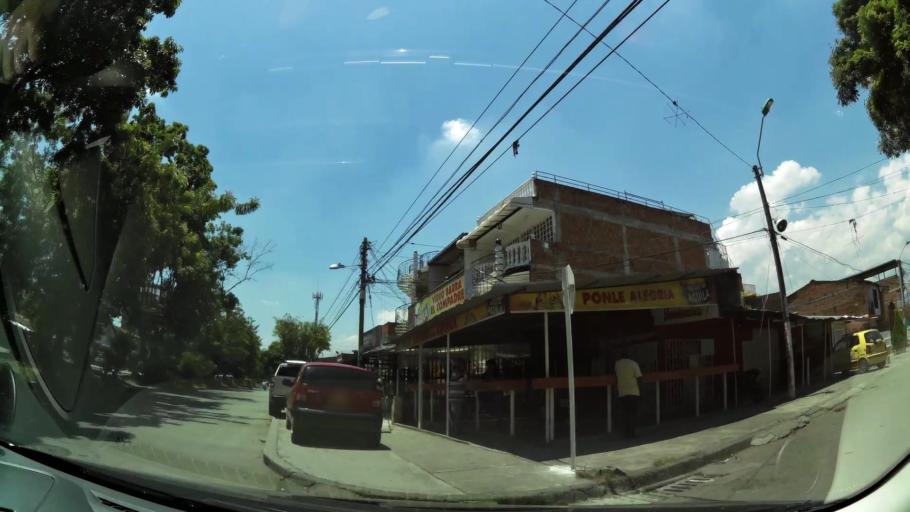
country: CO
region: Valle del Cauca
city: Cali
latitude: 3.4353
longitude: -76.5008
